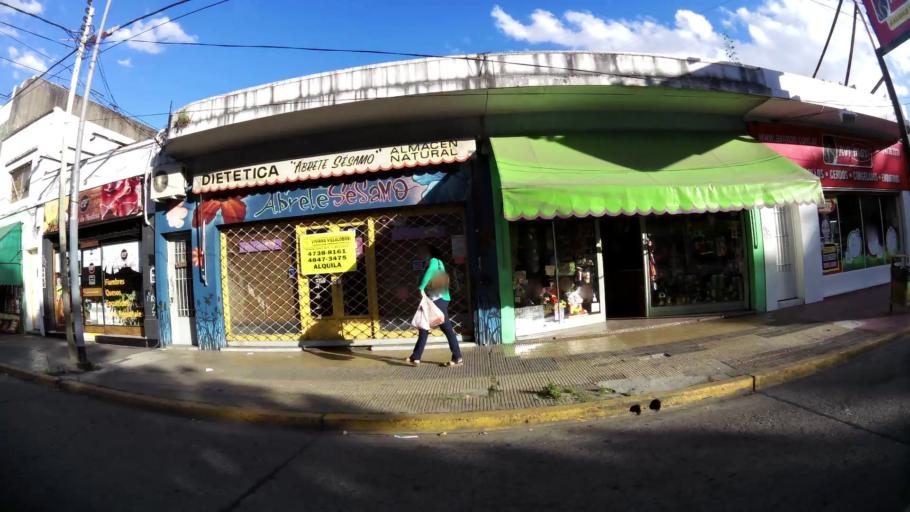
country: AR
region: Buenos Aires
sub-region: Partido de General San Martin
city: General San Martin
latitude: -34.5519
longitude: -58.5543
